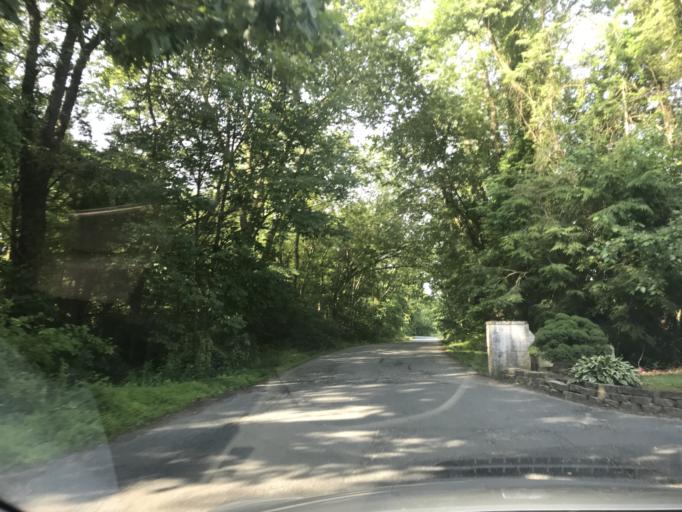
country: US
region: Maryland
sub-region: Harford County
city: Bel Air North
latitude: 39.5699
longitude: -76.3644
